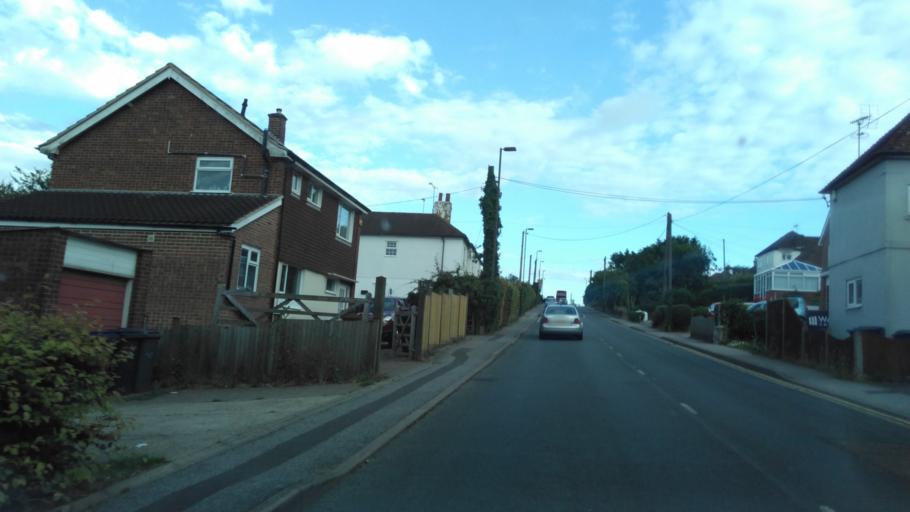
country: GB
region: England
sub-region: Kent
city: Blean
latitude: 51.3007
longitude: 1.0485
